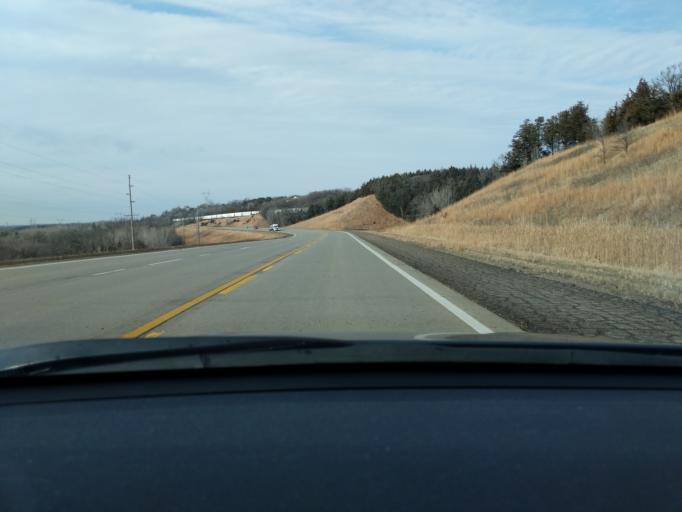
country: US
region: Minnesota
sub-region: Yellow Medicine County
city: Granite Falls
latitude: 44.7990
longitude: -95.5085
